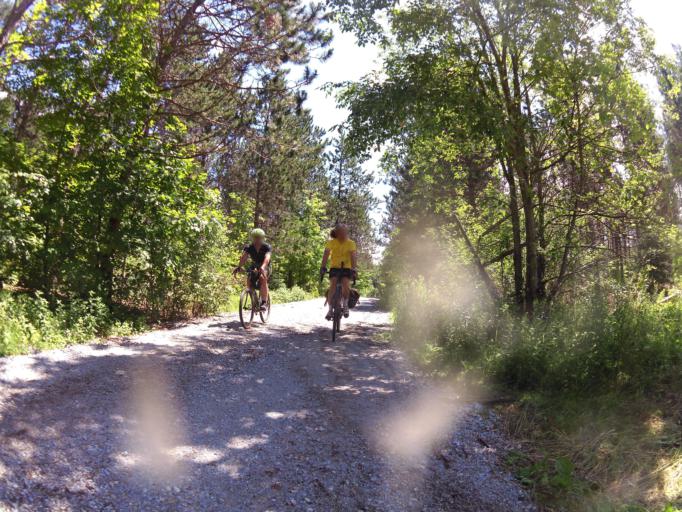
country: CA
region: Ontario
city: Perth
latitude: 45.0222
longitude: -76.6268
